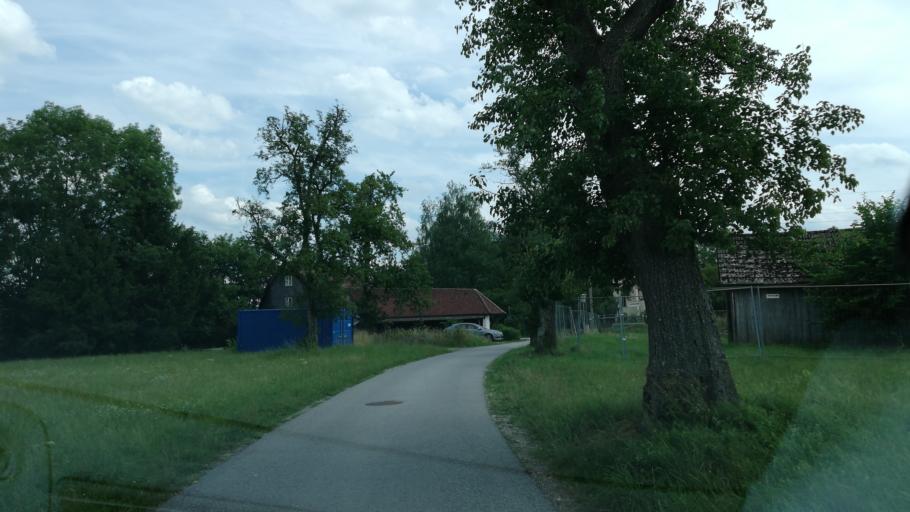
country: AT
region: Upper Austria
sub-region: Politischer Bezirk Vocklabruck
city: Attnang-Puchheim
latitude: 47.9932
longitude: 13.6873
